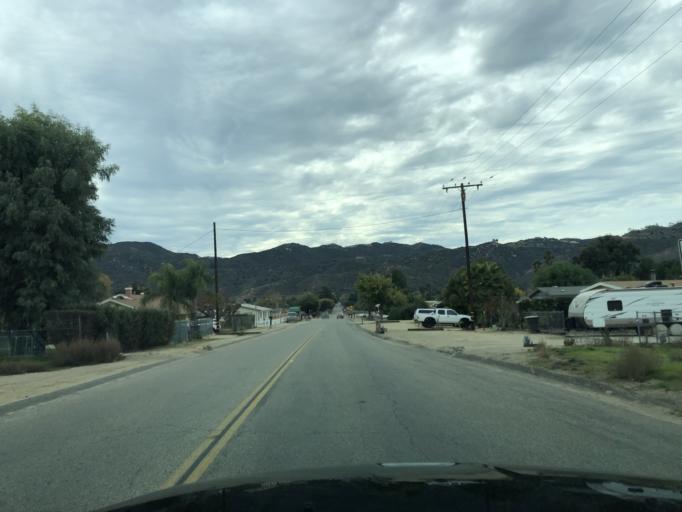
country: US
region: California
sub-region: Riverside County
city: Wildomar
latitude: 33.6058
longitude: -117.2766
